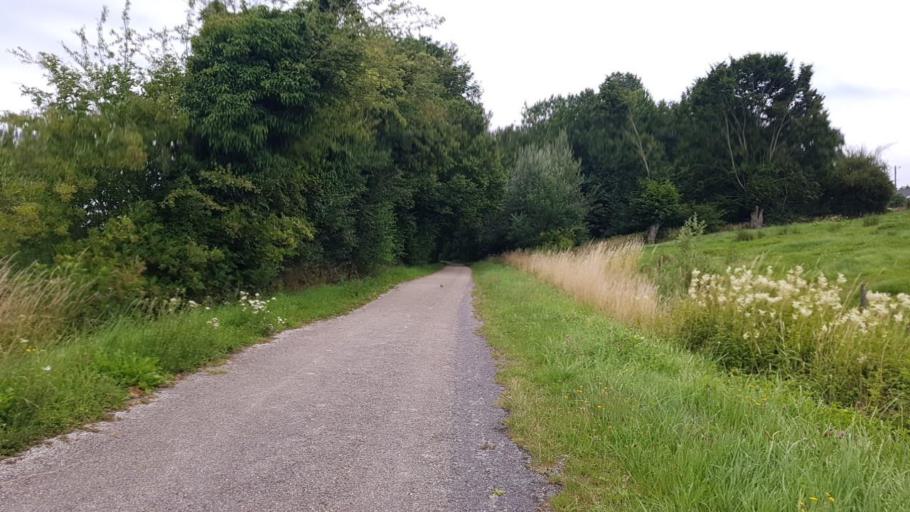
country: FR
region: Picardie
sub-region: Departement de l'Aisne
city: Esqueheries
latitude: 49.8993
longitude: 3.7283
